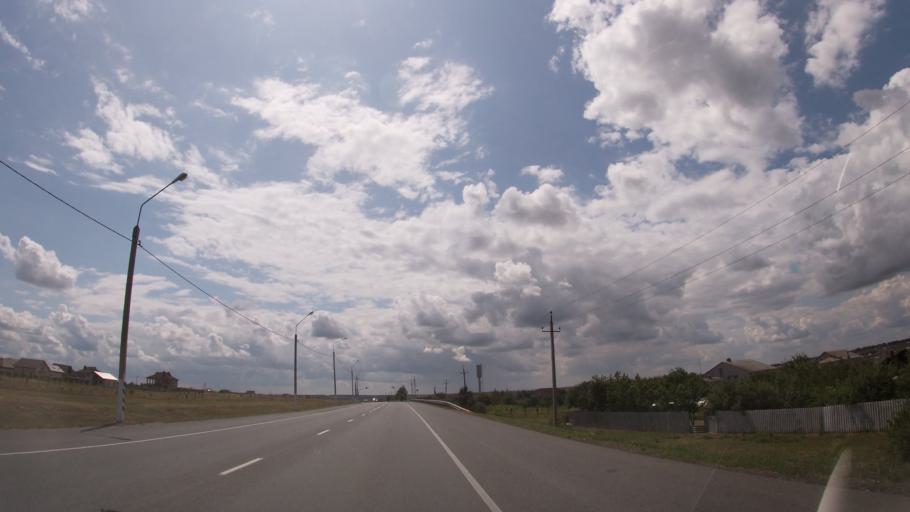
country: RU
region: Belgorod
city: Severnyy
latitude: 50.6547
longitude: 36.4672
